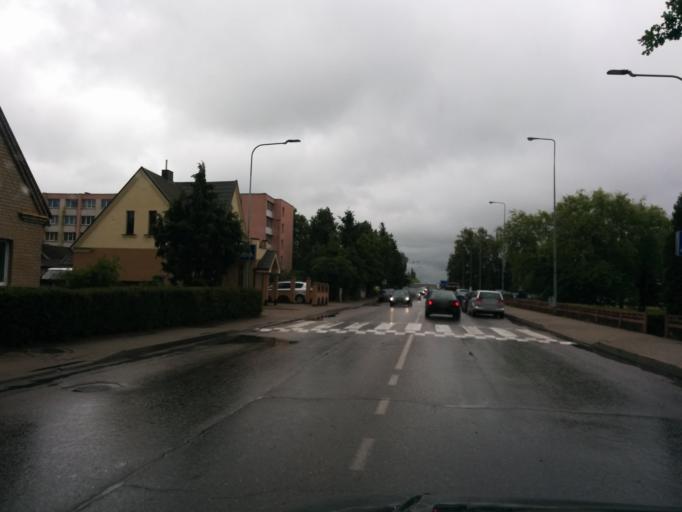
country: LT
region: Panevezys
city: Pasvalys
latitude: 56.0579
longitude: 24.4058
